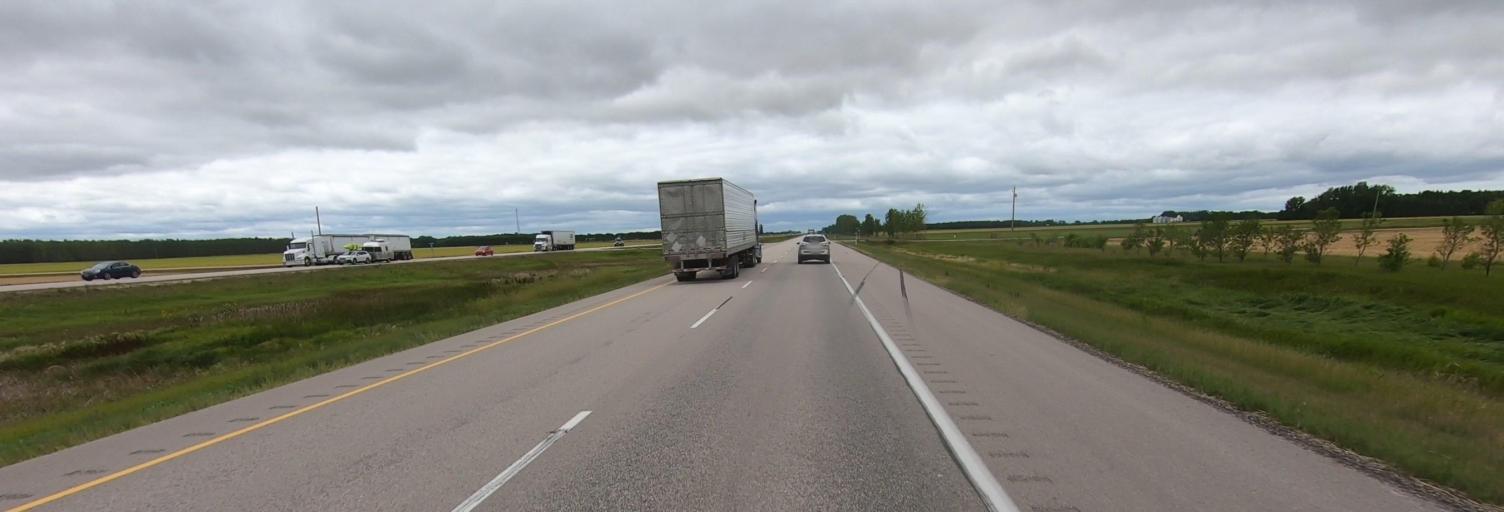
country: CA
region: Manitoba
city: Portage la Prairie
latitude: 49.9491
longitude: -97.9846
